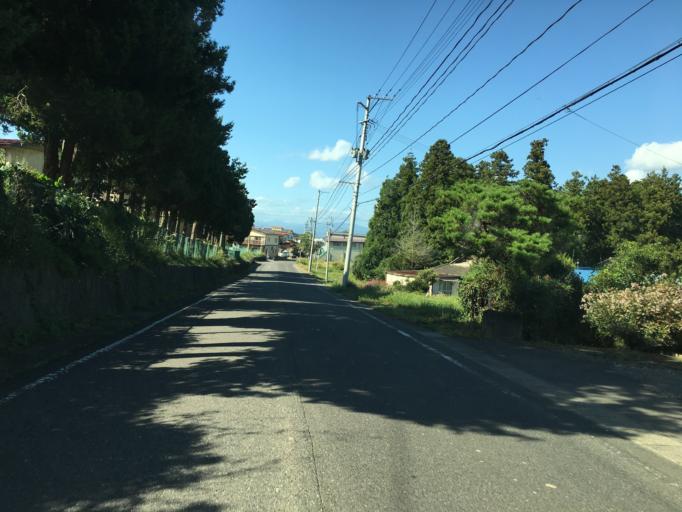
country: JP
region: Fukushima
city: Sukagawa
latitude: 37.2731
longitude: 140.3792
